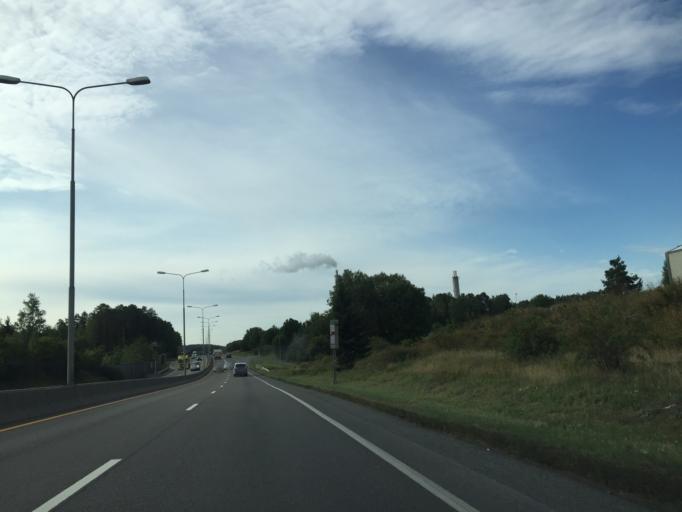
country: NO
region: Akershus
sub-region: Oppegard
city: Kolbotn
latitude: 59.8465
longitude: 10.8367
